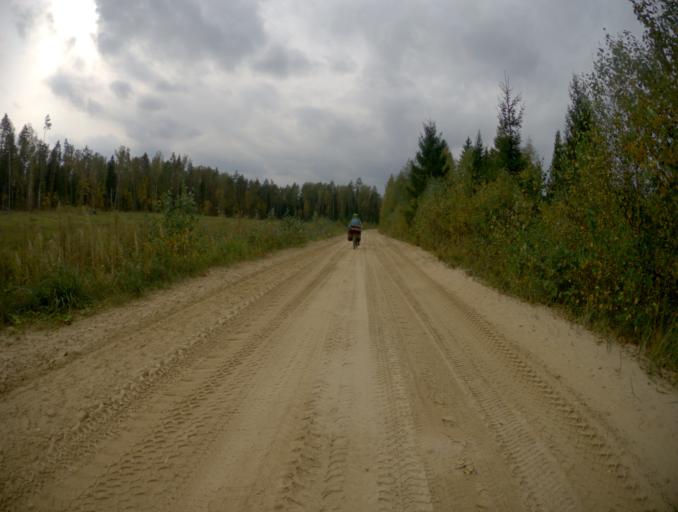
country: RU
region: Vladimir
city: Kideksha
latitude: 56.4695
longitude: 40.7073
